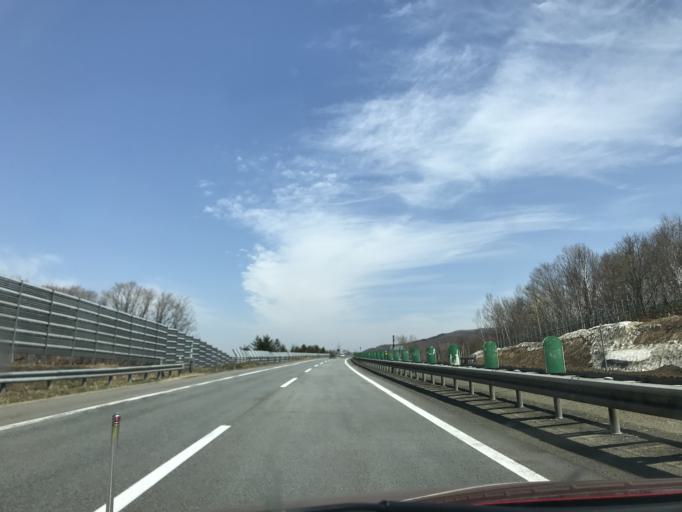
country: JP
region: Hokkaido
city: Bibai
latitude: 43.2611
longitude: 141.8366
